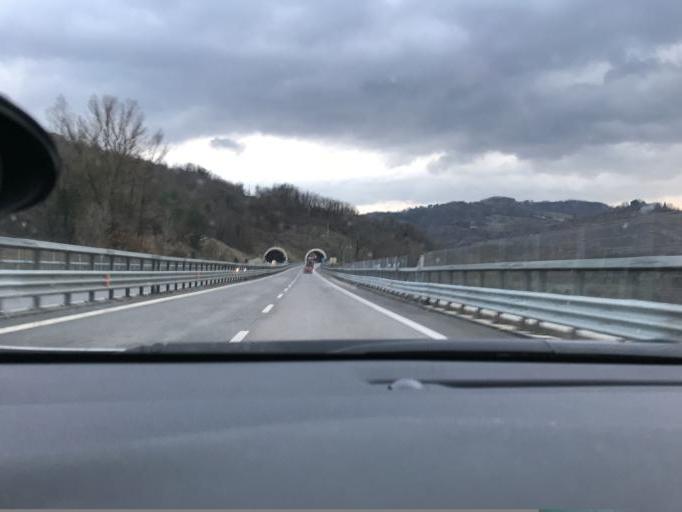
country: IT
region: Umbria
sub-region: Provincia di Perugia
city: Valfabbrica
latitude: 43.1809
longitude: 12.6147
